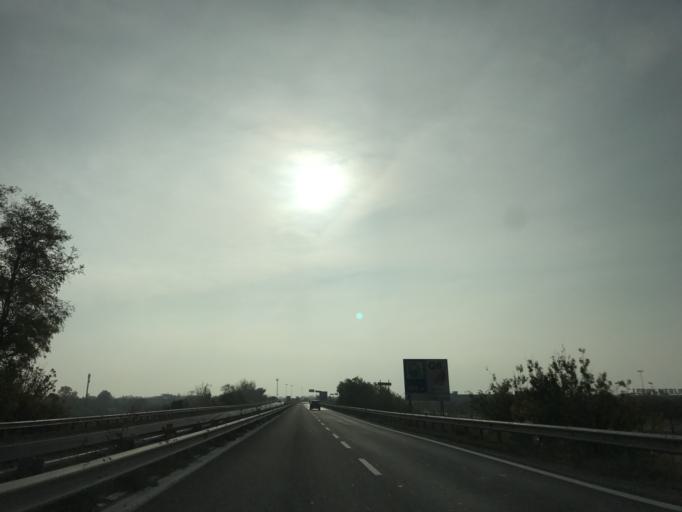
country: IT
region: Emilia-Romagna
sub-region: Forli-Cesena
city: Gatteo a Mare
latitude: 44.1613
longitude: 12.4322
